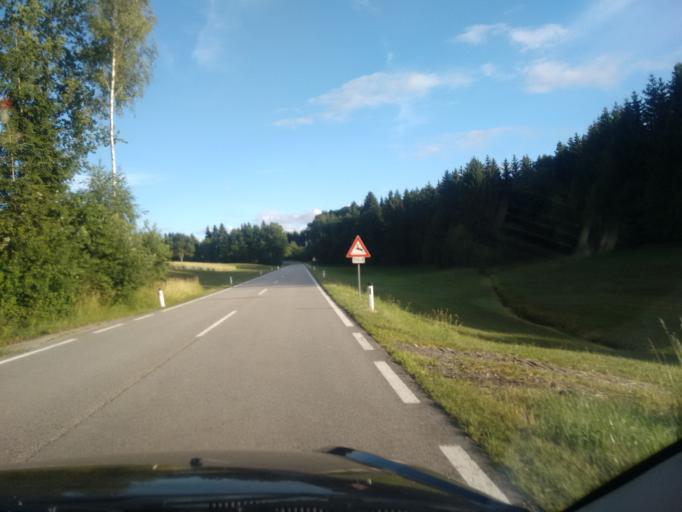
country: AT
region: Upper Austria
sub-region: Politischer Bezirk Urfahr-Umgebung
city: Gramastetten
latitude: 48.4176
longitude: 14.1625
